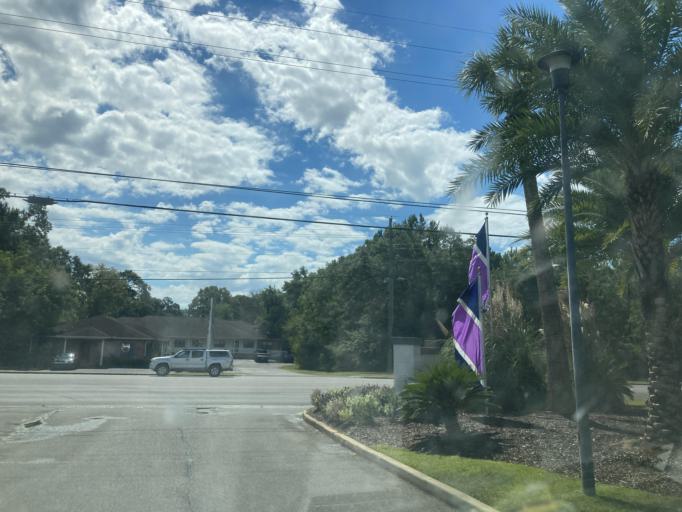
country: US
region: Mississippi
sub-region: Jackson County
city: Gulf Hills
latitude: 30.4434
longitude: -88.8524
